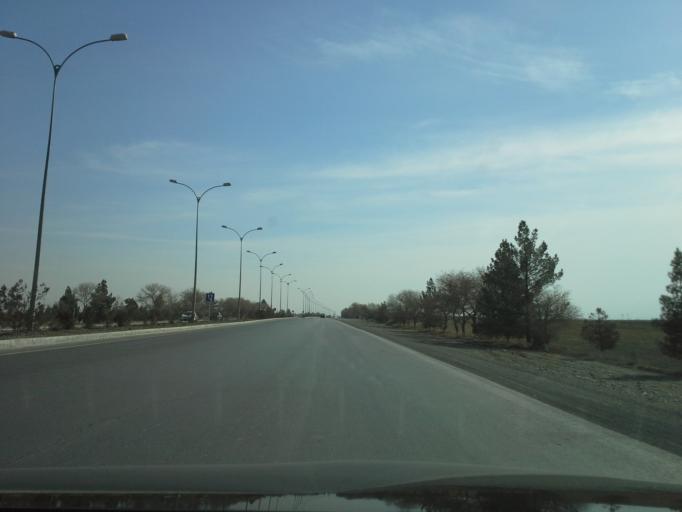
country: TM
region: Ahal
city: Abadan
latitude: 38.1257
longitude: 58.0325
